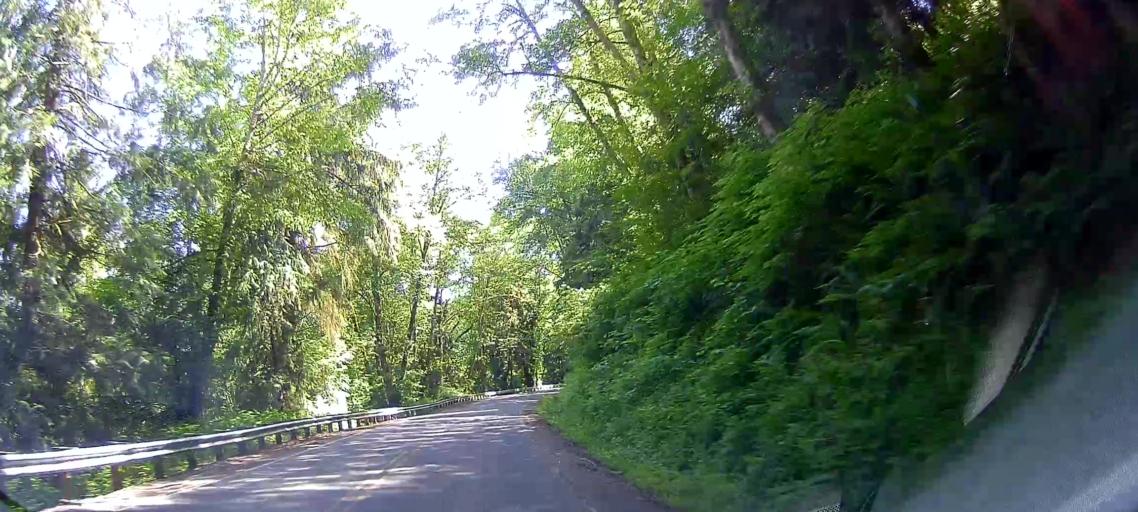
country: US
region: Washington
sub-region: Skagit County
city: Burlington
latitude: 48.5514
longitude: -122.3014
